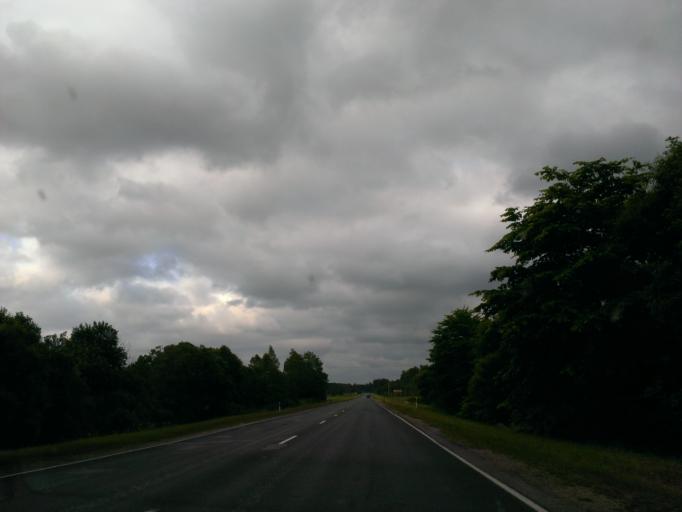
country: LV
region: Skrunda
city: Skrunda
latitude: 56.6796
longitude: 22.1320
